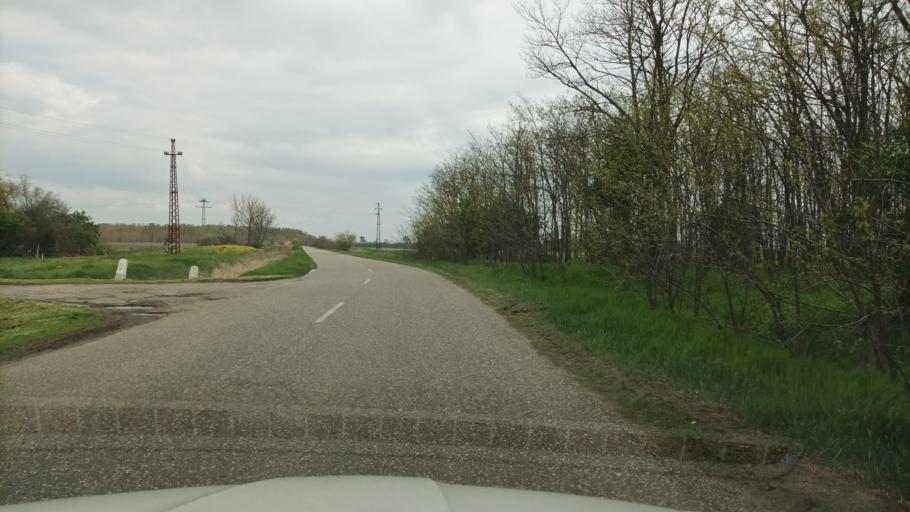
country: HU
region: Pest
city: Tortel
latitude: 47.1004
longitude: 19.9027
